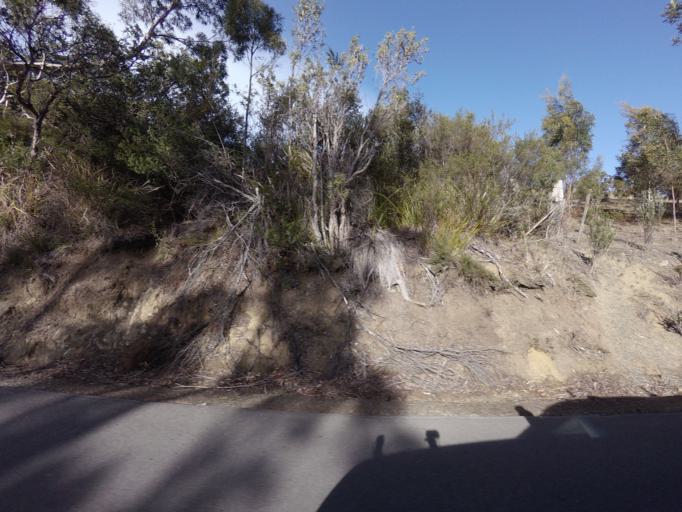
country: AU
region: Tasmania
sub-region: Kingborough
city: Kettering
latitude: -43.1671
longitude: 147.2103
